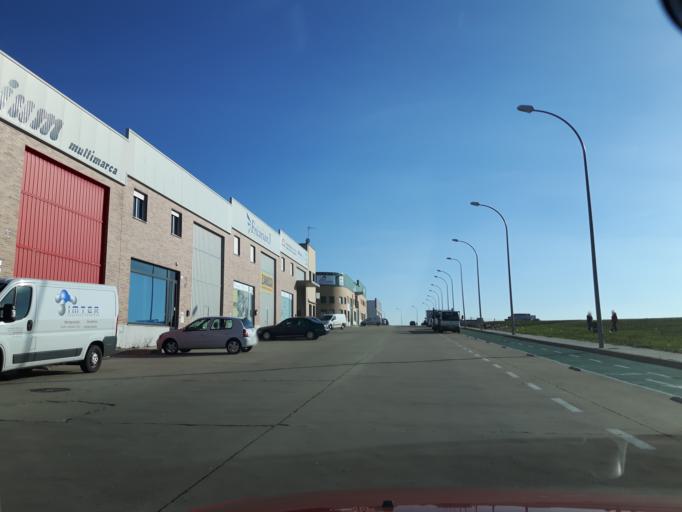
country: ES
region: Castille and Leon
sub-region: Provincia de Salamanca
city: Villares de la Reina
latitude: 40.9946
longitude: -5.6504
